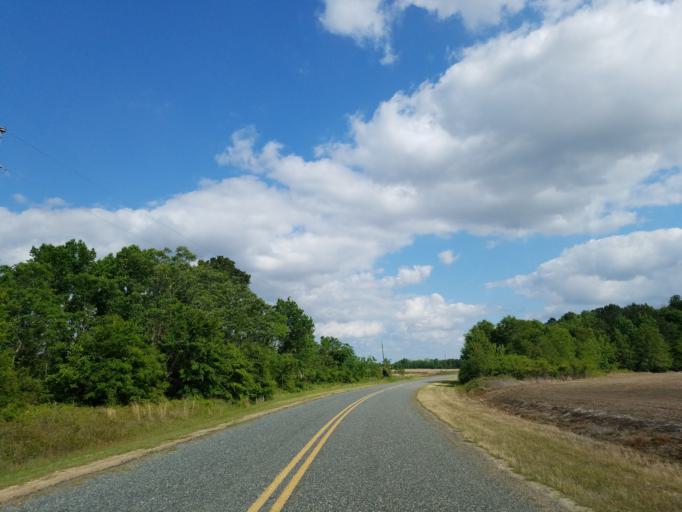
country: US
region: Georgia
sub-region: Dooly County
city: Unadilla
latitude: 32.2410
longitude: -83.7697
